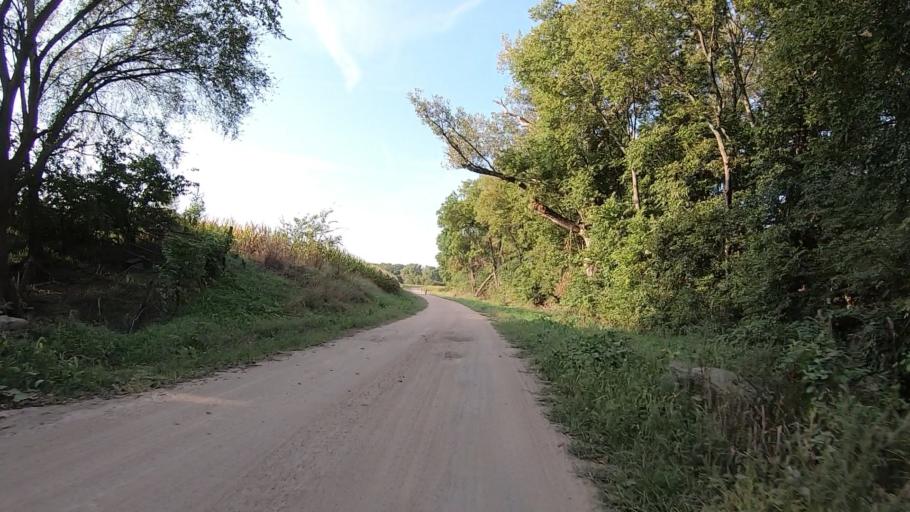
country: US
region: Kansas
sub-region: Marshall County
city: Blue Rapids
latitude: 39.7239
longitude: -96.7662
